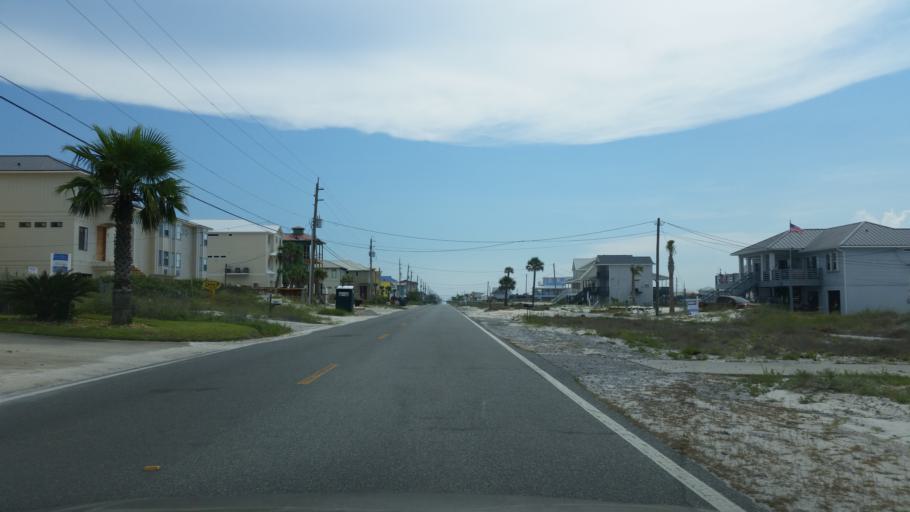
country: US
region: Florida
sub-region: Santa Rosa County
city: Navarre
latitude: 30.3754
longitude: -86.8966
